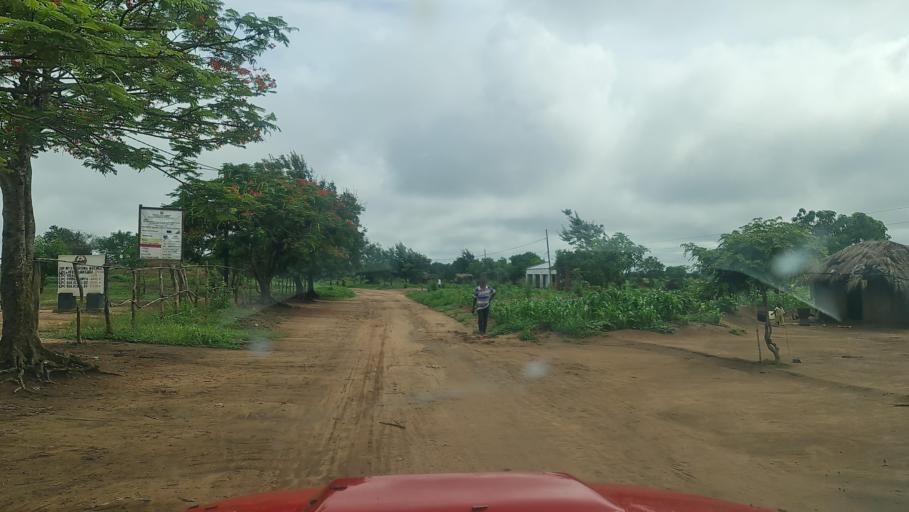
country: MW
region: Southern Region
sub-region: Nsanje District
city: Nsanje
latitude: -17.2203
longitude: 35.6729
